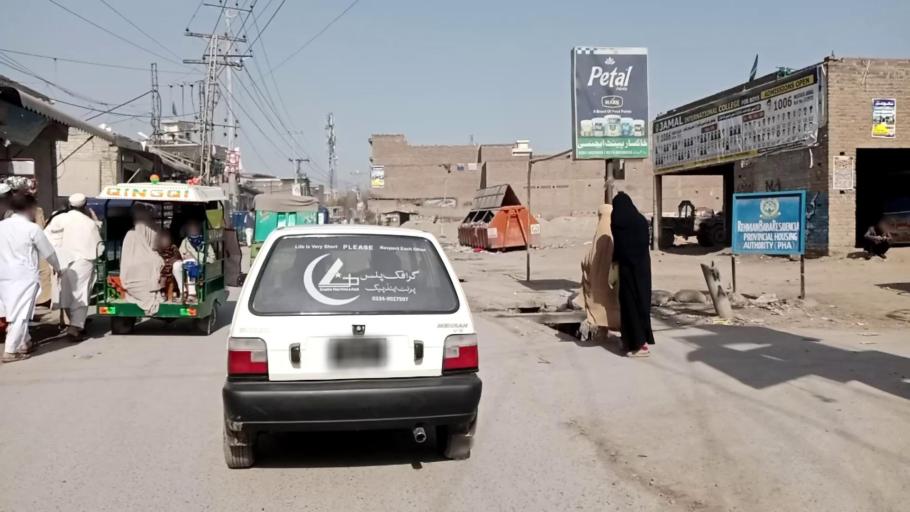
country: PK
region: Khyber Pakhtunkhwa
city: Peshawar
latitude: 33.9940
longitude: 71.5793
